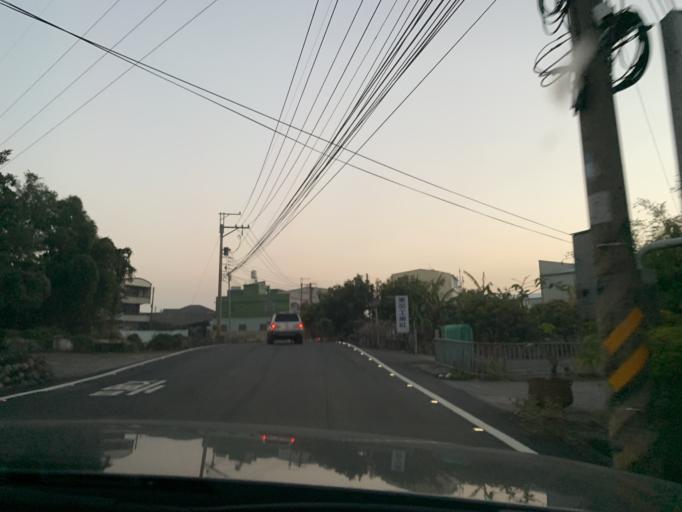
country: TW
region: Taiwan
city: Fengyuan
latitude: 24.2703
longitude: 120.7327
